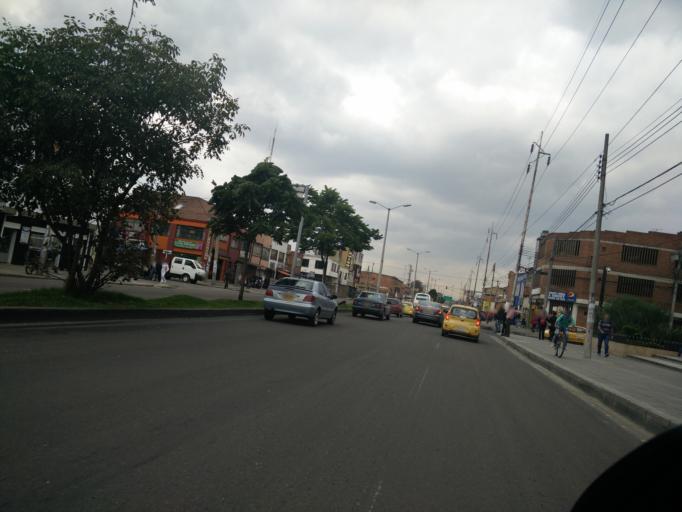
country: CO
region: Bogota D.C.
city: Bogota
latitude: 4.6512
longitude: -74.0731
